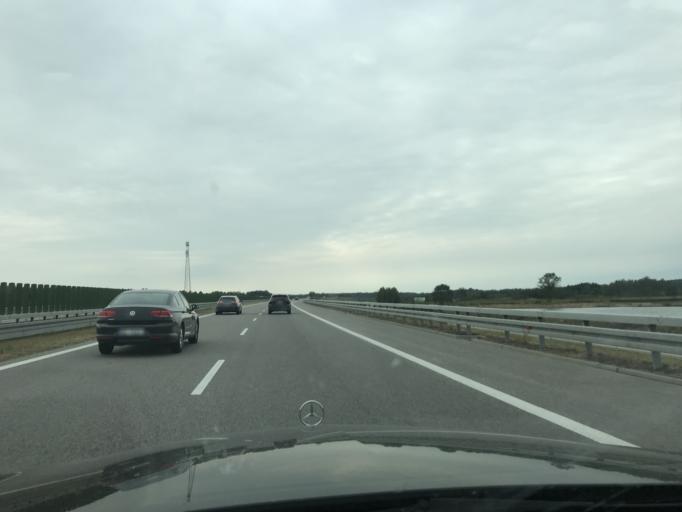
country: PL
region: Subcarpathian Voivodeship
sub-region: Powiat ropczycko-sedziszowski
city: Sedziszow Malopolski
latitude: 50.1129
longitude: 21.7595
